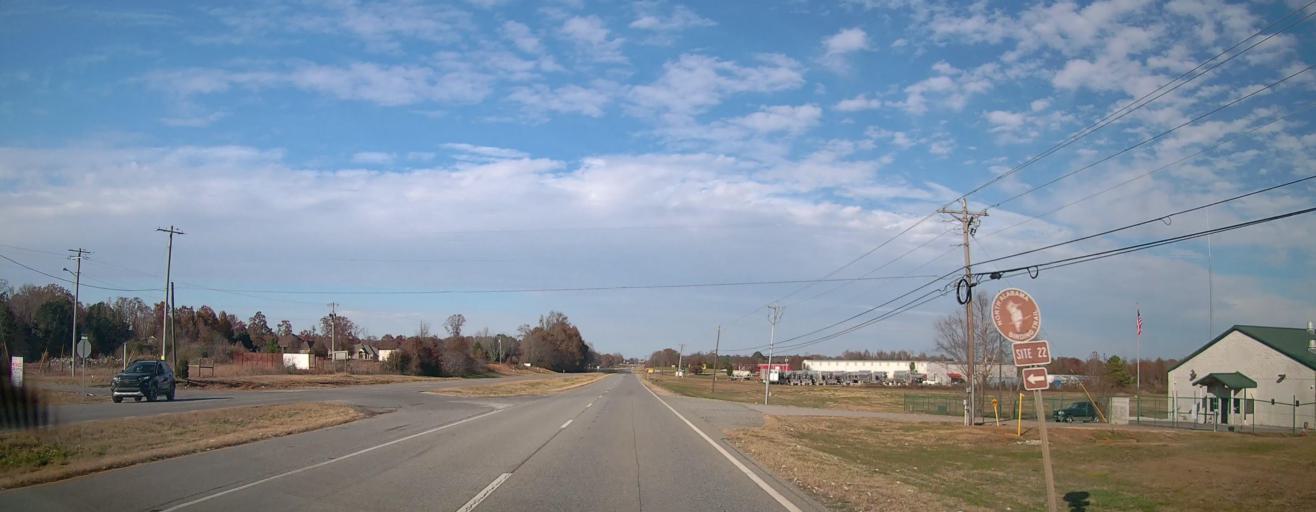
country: US
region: Alabama
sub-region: Limestone County
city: Athens
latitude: 34.7165
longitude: -86.9563
